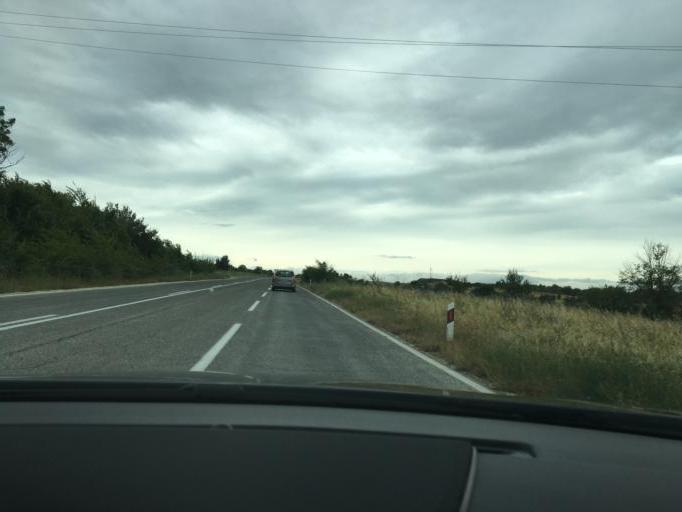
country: MK
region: Staro Nagoricane
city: Staro Nagorichane
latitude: 42.1678
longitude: 21.8291
